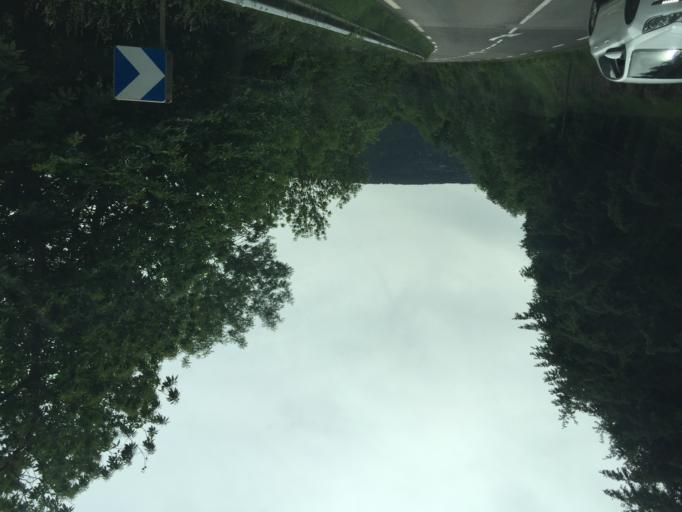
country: FR
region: Rhone-Alpes
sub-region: Departement de la Loire
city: Bourg-Argental
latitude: 45.2982
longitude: 4.5410
